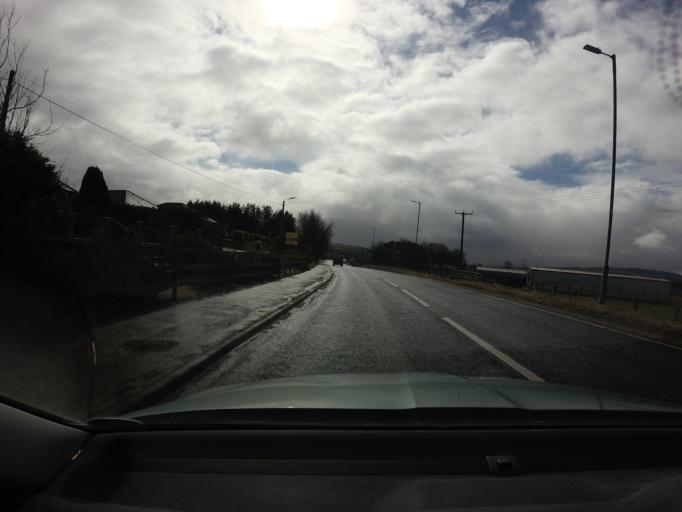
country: GB
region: Scotland
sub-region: South Lanarkshire
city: Douglas
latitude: 55.5929
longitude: -3.7930
